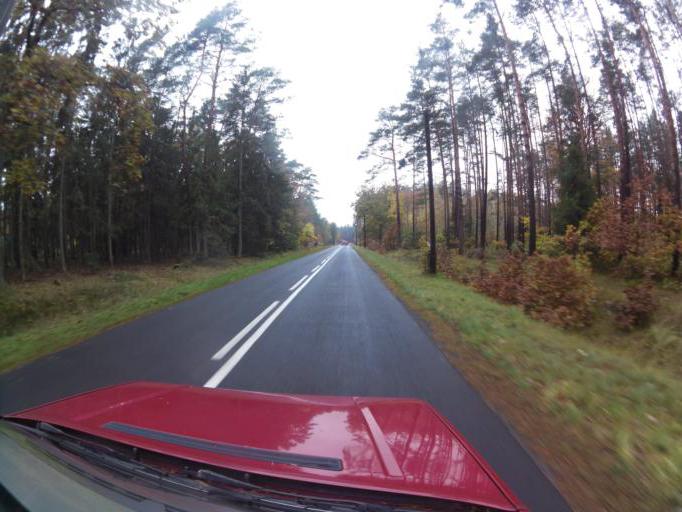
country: PL
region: West Pomeranian Voivodeship
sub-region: Powiat policki
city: Dobra
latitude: 53.5948
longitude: 14.3550
